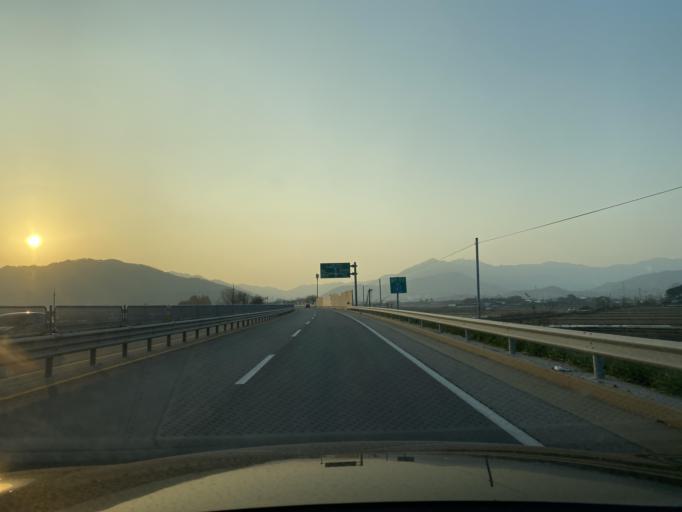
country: KR
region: Chungcheongnam-do
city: Hongsung
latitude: 36.6909
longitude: 126.6921
